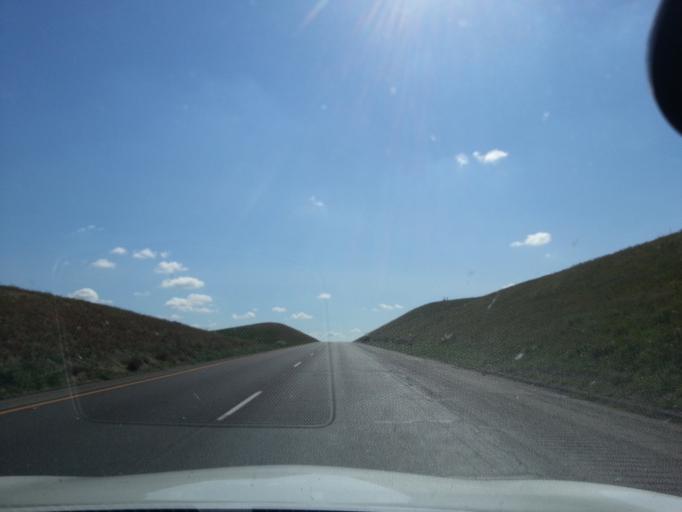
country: US
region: California
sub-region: Fresno County
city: Coalinga
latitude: 36.3238
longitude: -120.2945
